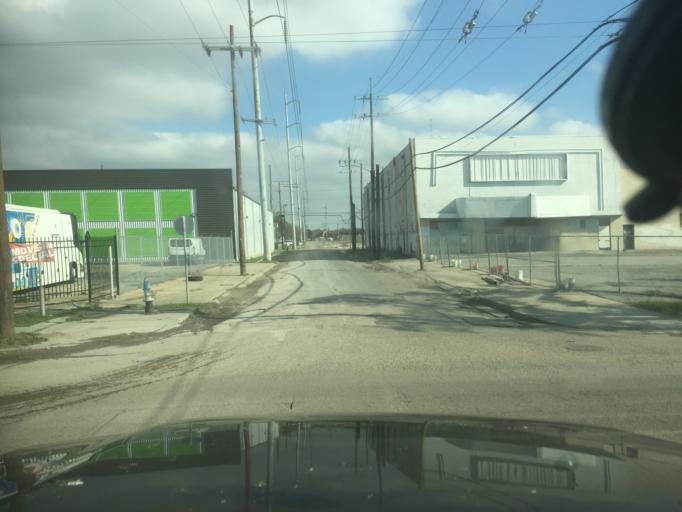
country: US
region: Louisiana
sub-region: Orleans Parish
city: New Orleans
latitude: 29.9890
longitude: -90.0494
